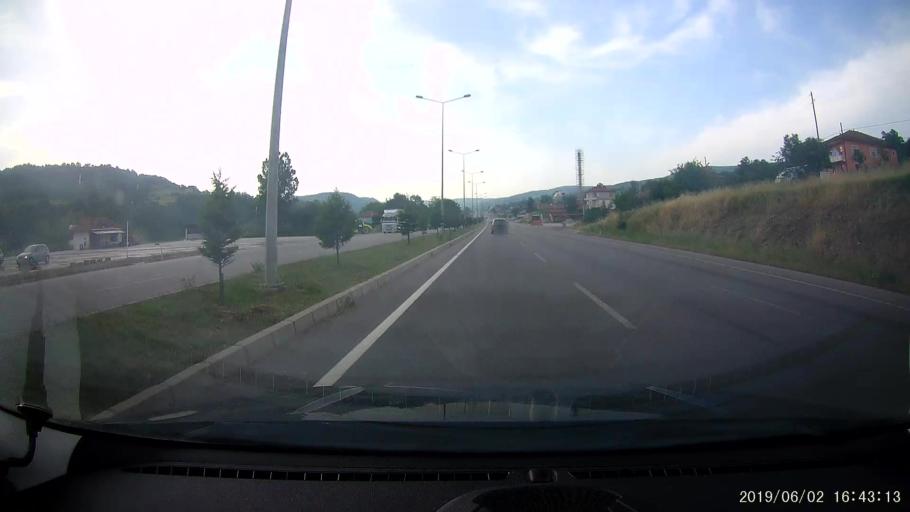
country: TR
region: Samsun
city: Kavak
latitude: 41.1317
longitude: 36.1315
